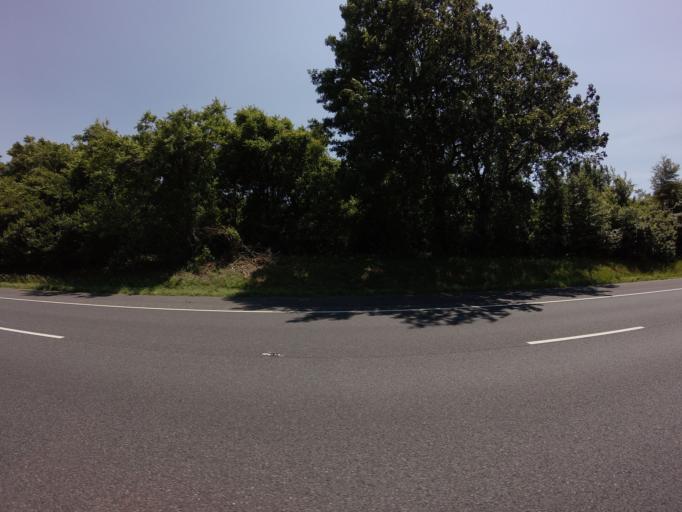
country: US
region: Maryland
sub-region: Frederick County
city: Ballenger Creek
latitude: 39.3979
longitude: -77.4313
